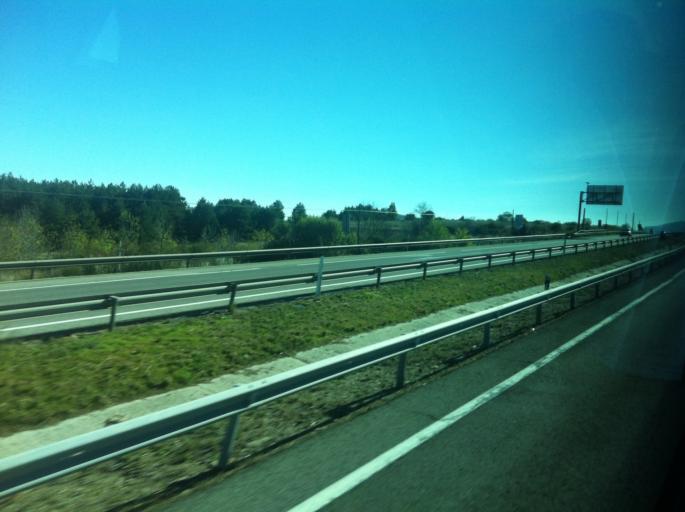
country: ES
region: Madrid
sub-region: Provincia de Madrid
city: Horcajo de la Sierra
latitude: 41.0574
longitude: -3.6129
